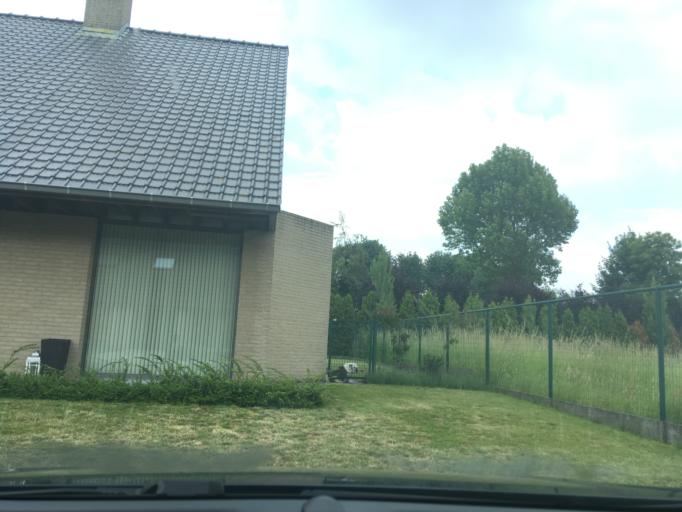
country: BE
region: Flanders
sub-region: Provincie West-Vlaanderen
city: Meulebeke
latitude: 50.9477
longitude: 3.3023
